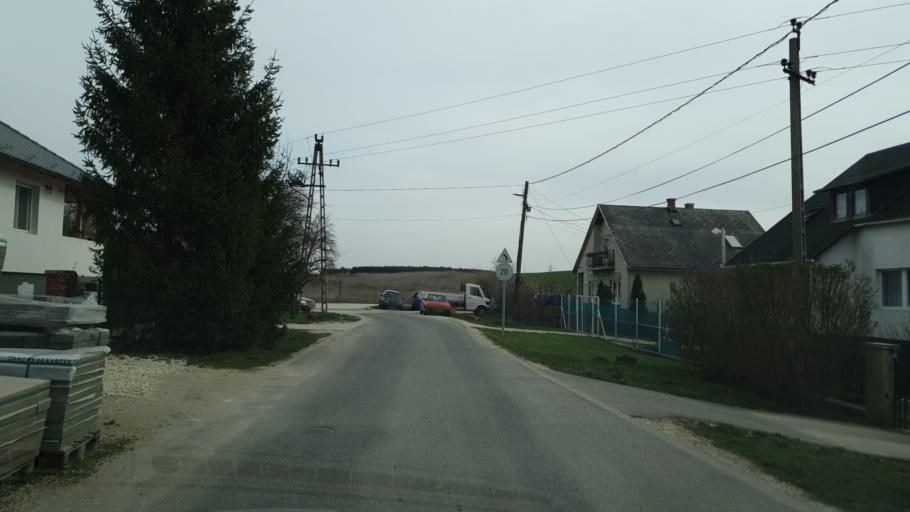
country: HU
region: Fejer
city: Etyek
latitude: 47.4404
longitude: 18.7558
